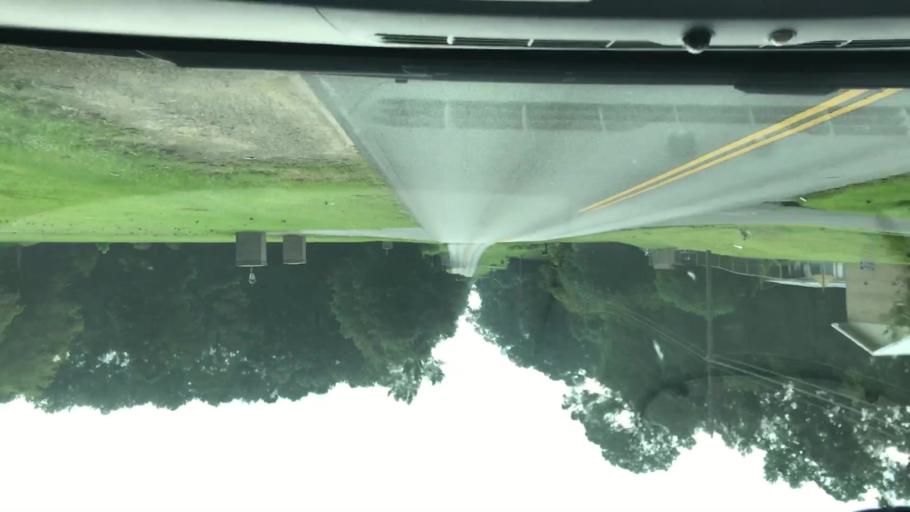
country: US
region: Florida
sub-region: Jackson County
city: Marianna
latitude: 30.7689
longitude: -85.2371
